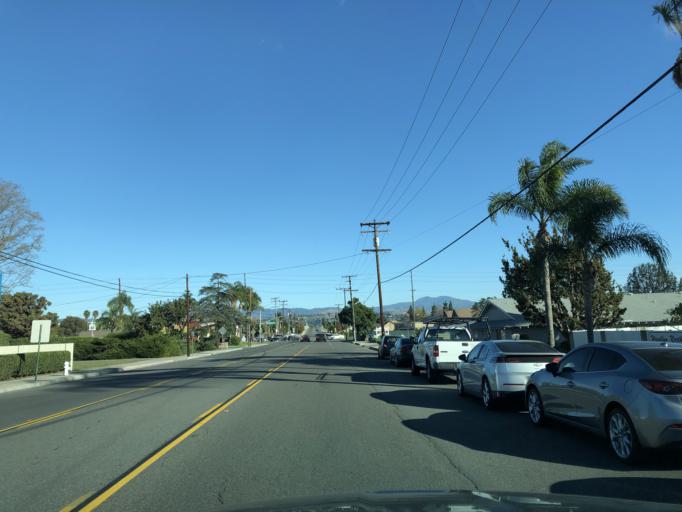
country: US
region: California
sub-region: Orange County
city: Tustin
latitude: 33.7671
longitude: -117.8376
